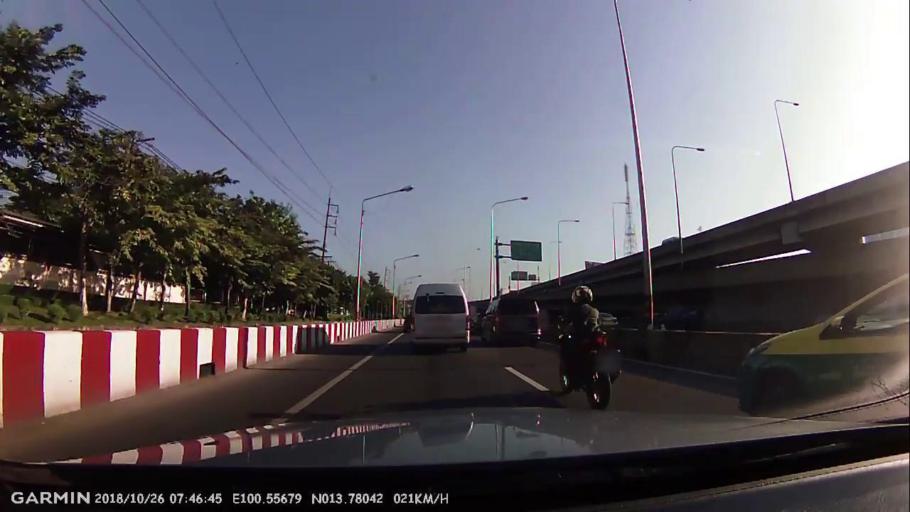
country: TH
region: Bangkok
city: Din Daeng
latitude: 13.7804
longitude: 100.5568
